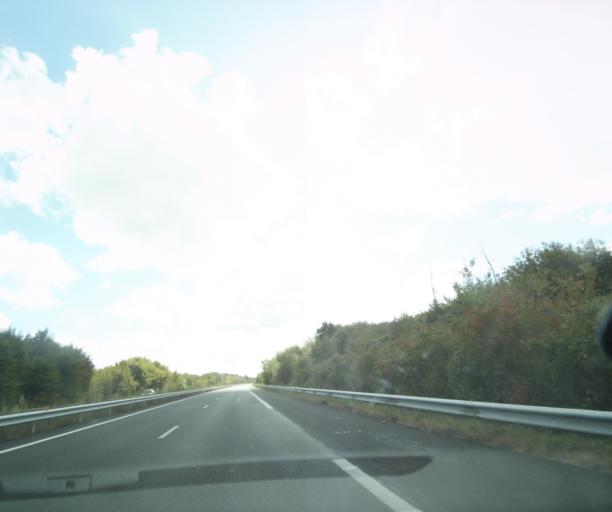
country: FR
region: Poitou-Charentes
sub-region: Departement de la Charente-Maritime
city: Bords
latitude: 45.9046
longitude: -0.7679
